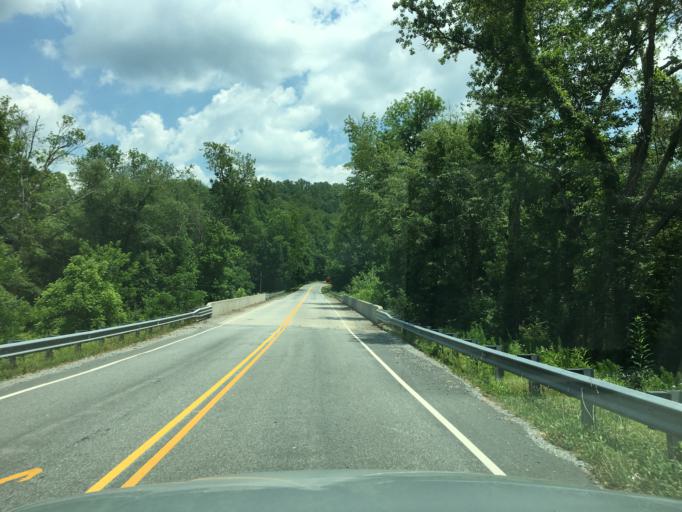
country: US
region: North Carolina
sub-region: Rutherford County
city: Rutherfordton
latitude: 35.3424
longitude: -82.0106
